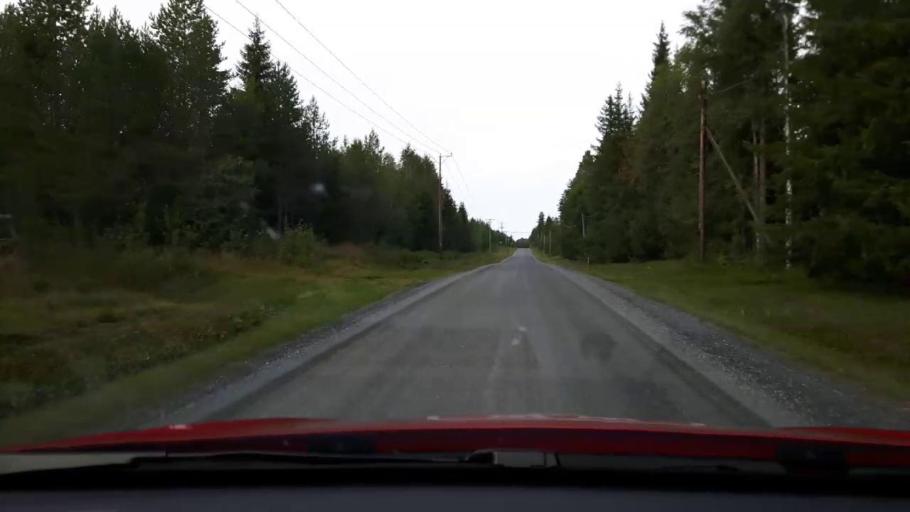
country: SE
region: Jaemtland
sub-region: Krokoms Kommun
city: Valla
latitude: 63.2484
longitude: 13.9611
